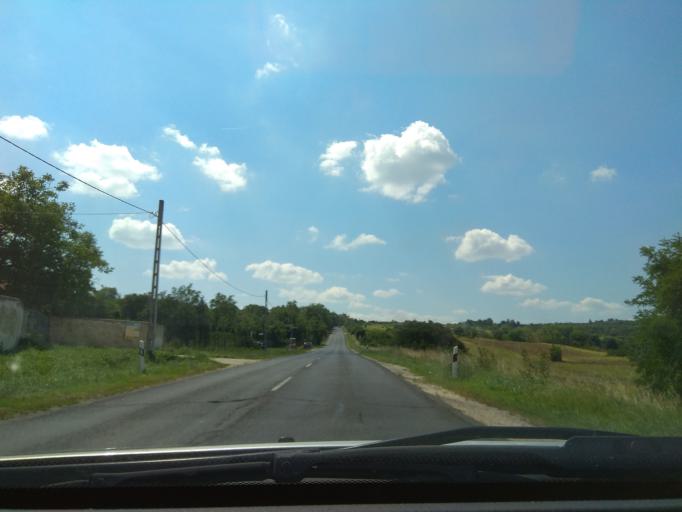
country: HU
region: Borsod-Abauj-Zemplen
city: Malyi
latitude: 48.0438
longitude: 20.7897
